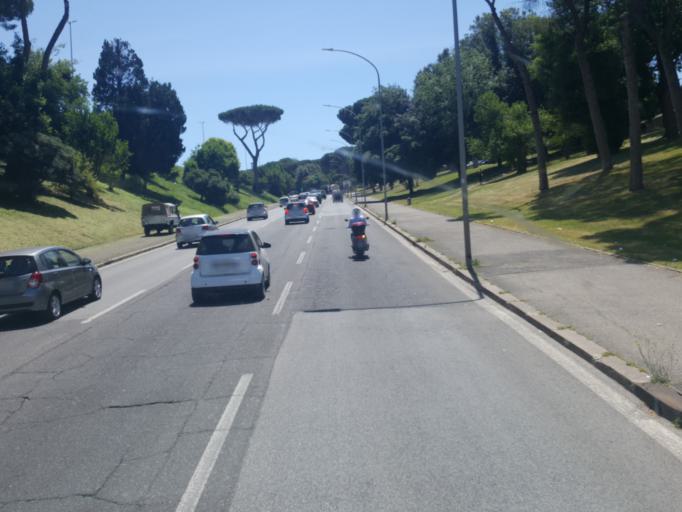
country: IT
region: Latium
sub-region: Citta metropolitana di Roma Capitale
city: Selcetta
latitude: 41.8267
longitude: 12.4654
